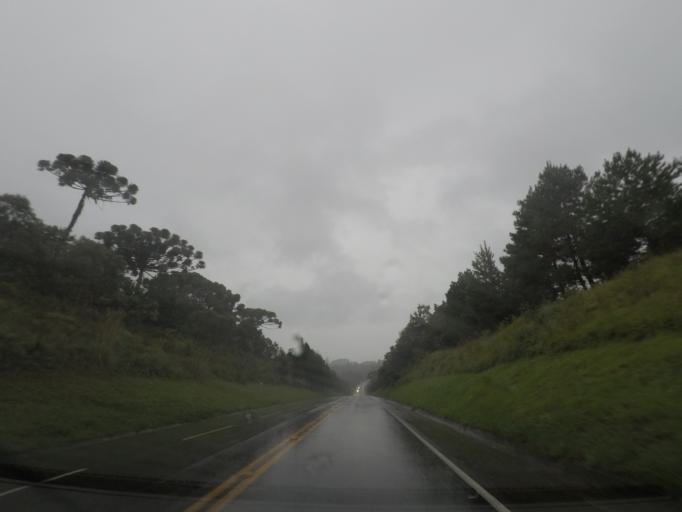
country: BR
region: Parana
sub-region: Almirante Tamandare
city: Almirante Tamandare
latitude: -25.3583
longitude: -49.3114
